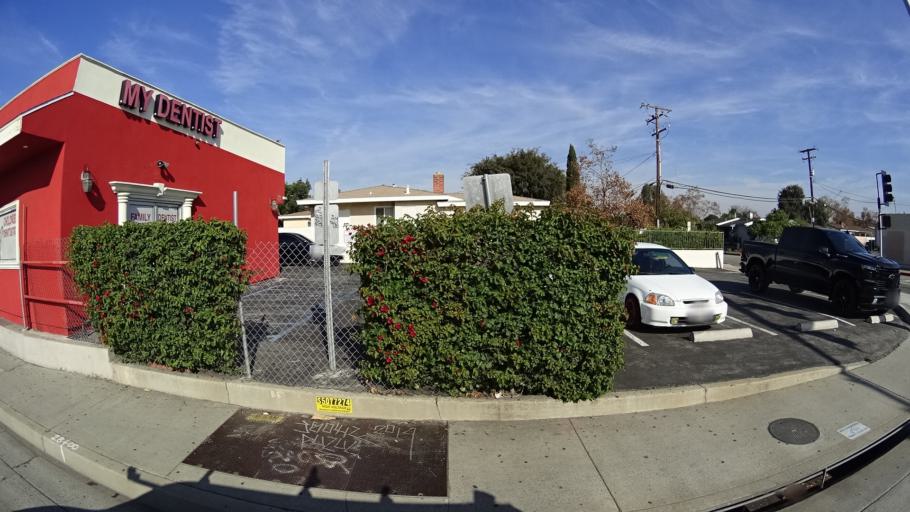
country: US
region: California
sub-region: Orange County
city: Santa Ana
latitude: 33.7600
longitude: -117.8968
